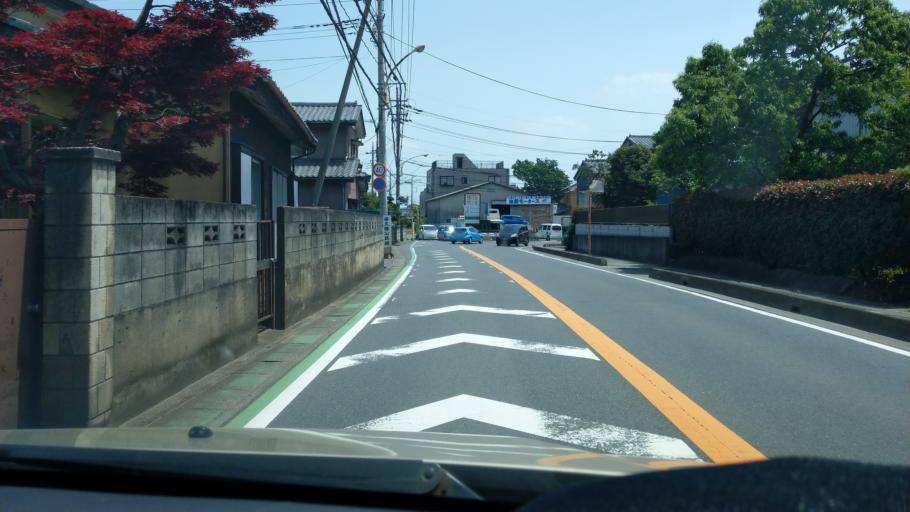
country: JP
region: Saitama
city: Iwatsuki
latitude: 35.9182
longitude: 139.7212
